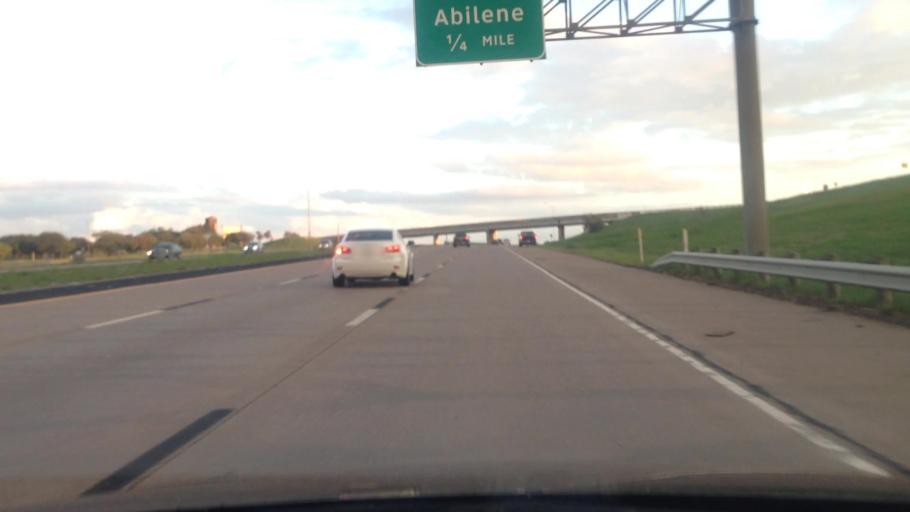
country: US
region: Texas
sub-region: Tarrant County
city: Benbrook
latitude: 32.7051
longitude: -97.4743
